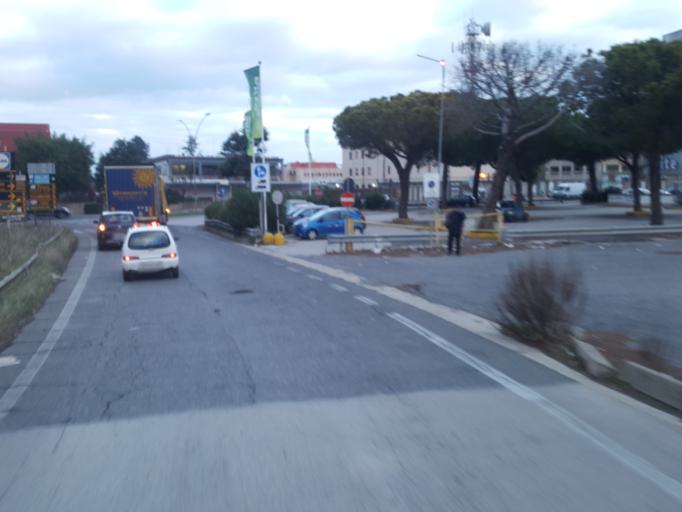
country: IT
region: Latium
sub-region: Citta metropolitana di Roma Capitale
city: Area Produttiva
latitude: 41.6769
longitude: 12.5005
